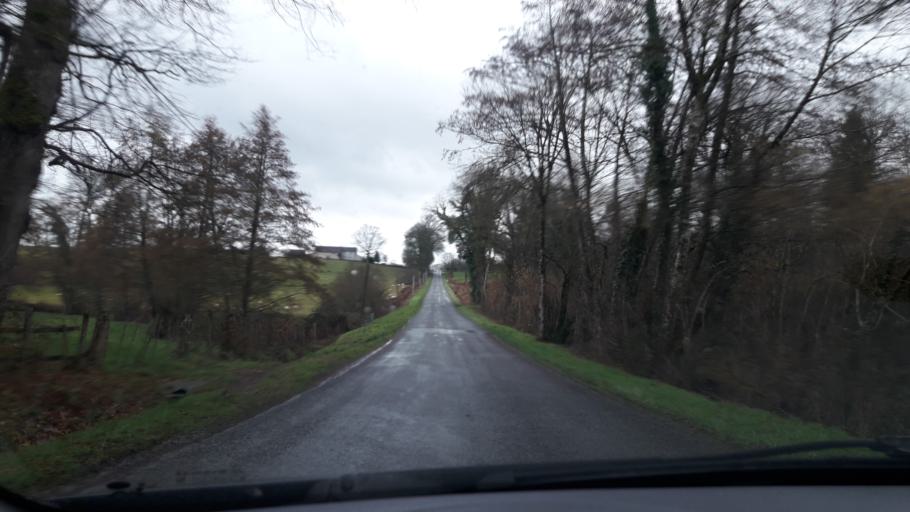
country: FR
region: Limousin
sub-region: Departement de la Haute-Vienne
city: Saint-Paul
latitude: 45.7844
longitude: 1.4492
